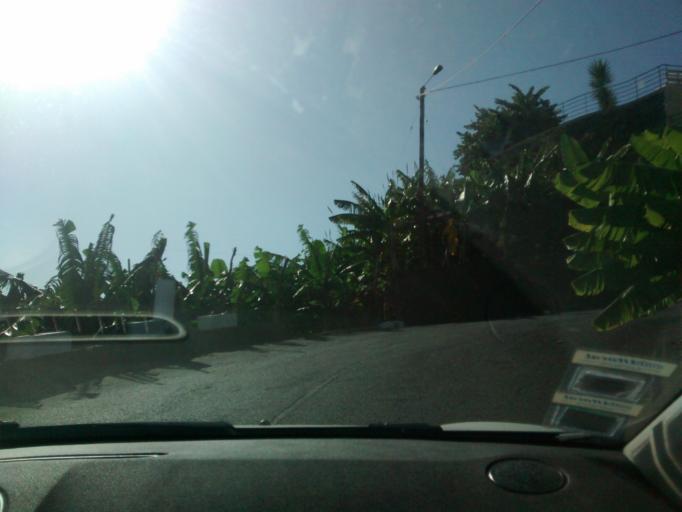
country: PT
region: Madeira
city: Calheta
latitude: 32.7186
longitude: -17.1698
